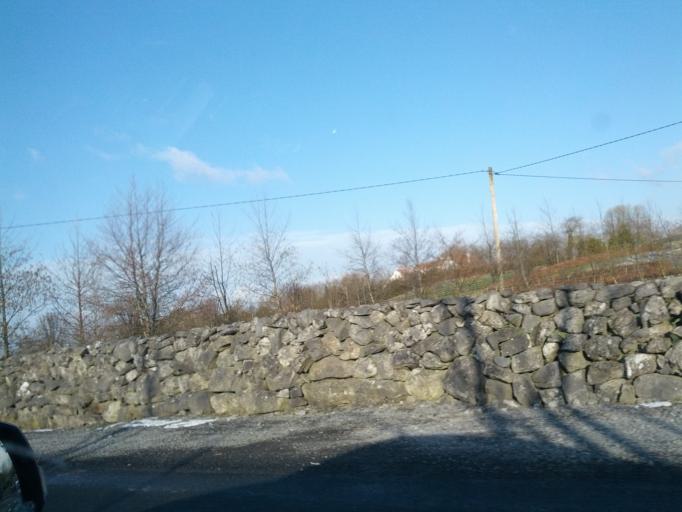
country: IE
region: Connaught
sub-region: County Galway
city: Gort
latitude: 53.1571
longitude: -8.7834
